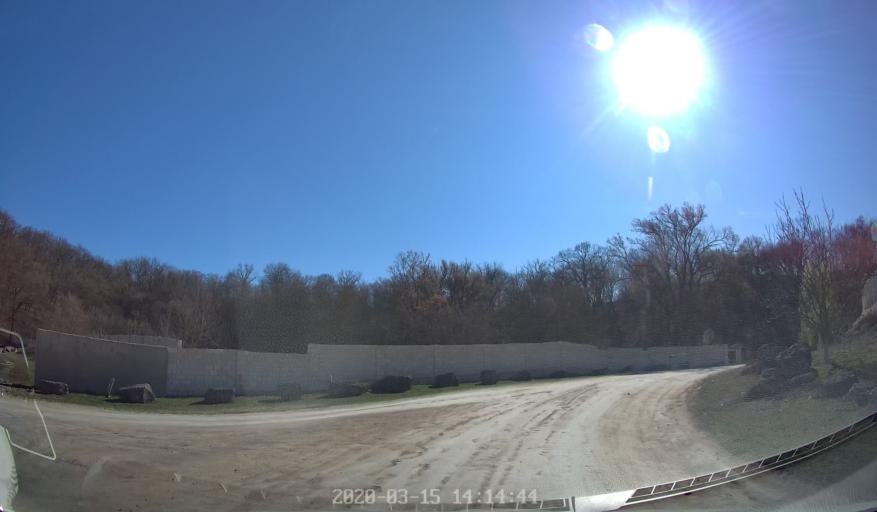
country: MD
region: Orhei
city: Orhei
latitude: 47.3124
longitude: 28.9364
